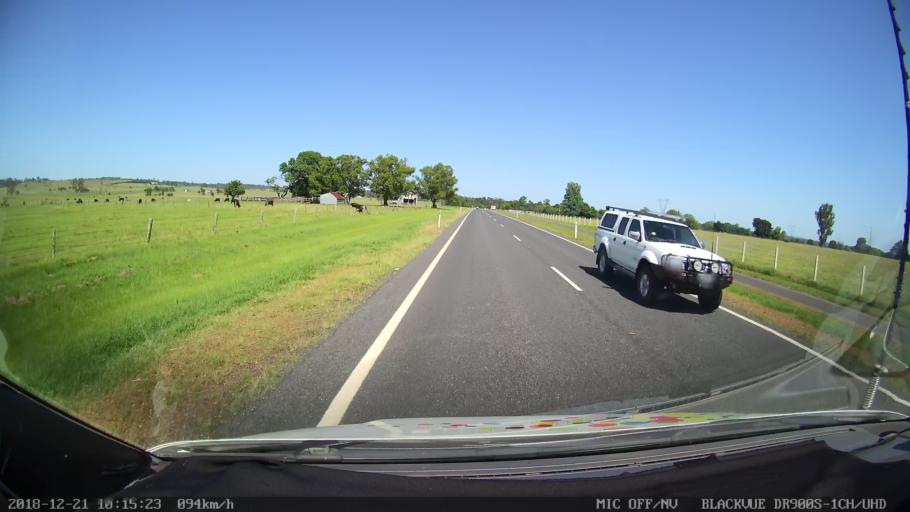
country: AU
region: New South Wales
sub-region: Clarence Valley
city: South Grafton
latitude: -29.6897
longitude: 152.9007
